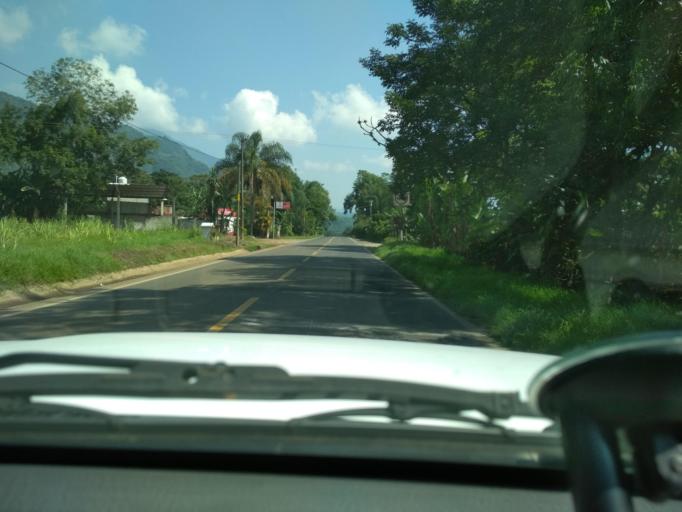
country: MX
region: Veracruz
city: Monte Blanco
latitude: 18.9761
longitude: -97.0162
